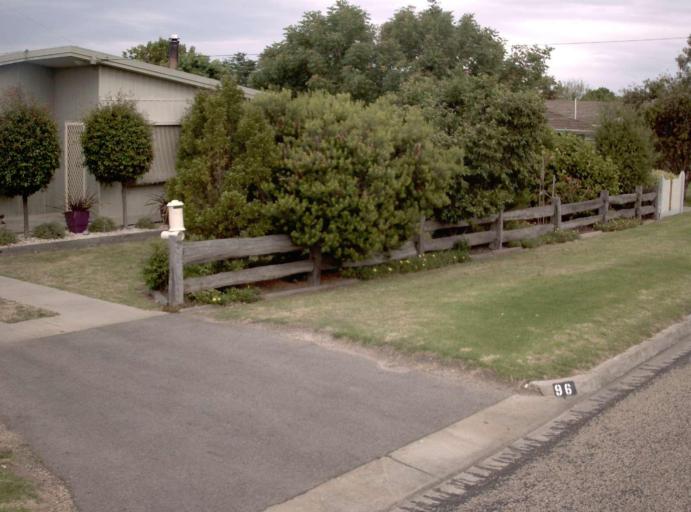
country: AU
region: Victoria
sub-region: East Gippsland
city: Bairnsdale
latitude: -37.9108
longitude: 147.7201
